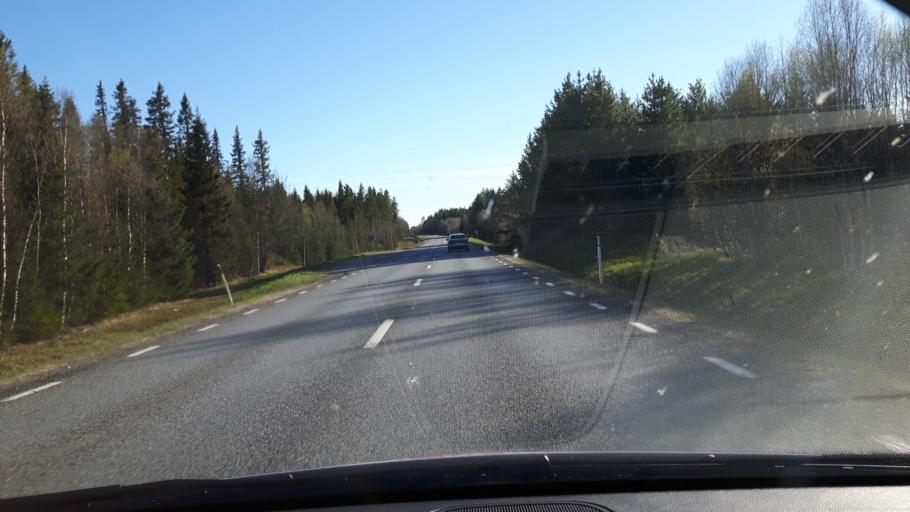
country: SE
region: Jaemtland
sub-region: OEstersunds Kommun
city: Lit
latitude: 63.4504
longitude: 15.1574
